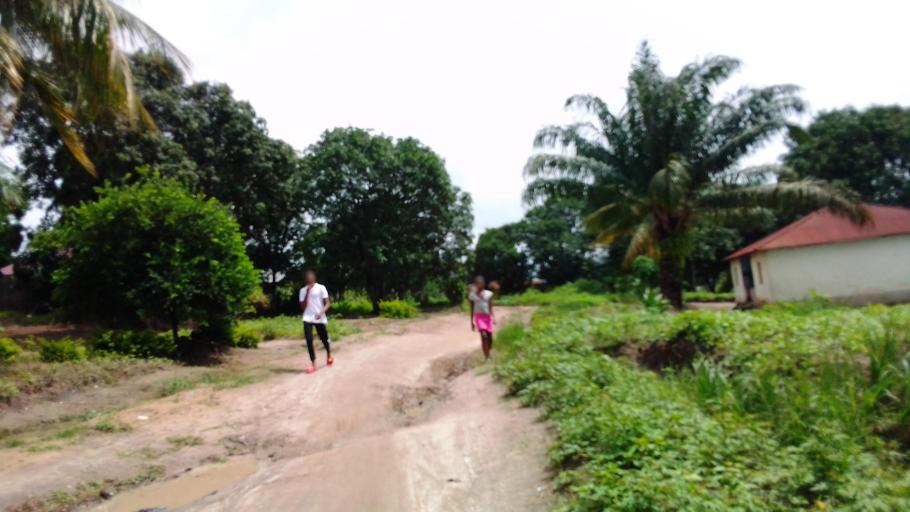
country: SL
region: Eastern Province
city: Kenema
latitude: 7.8643
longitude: -11.1763
